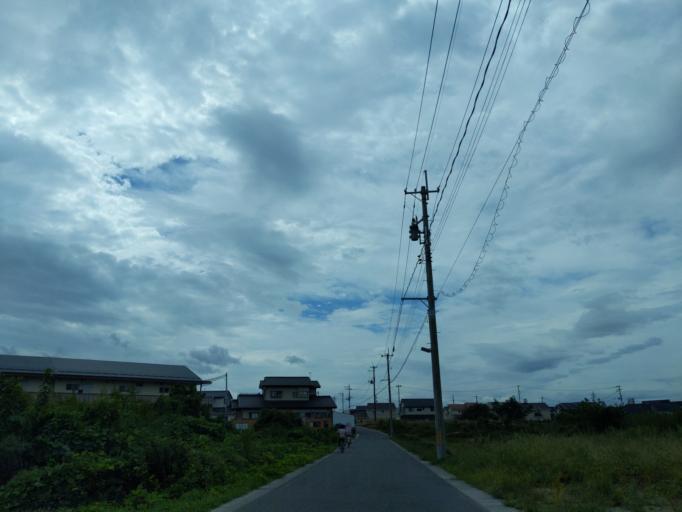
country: JP
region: Fukushima
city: Koriyama
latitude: 37.4002
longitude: 140.4047
